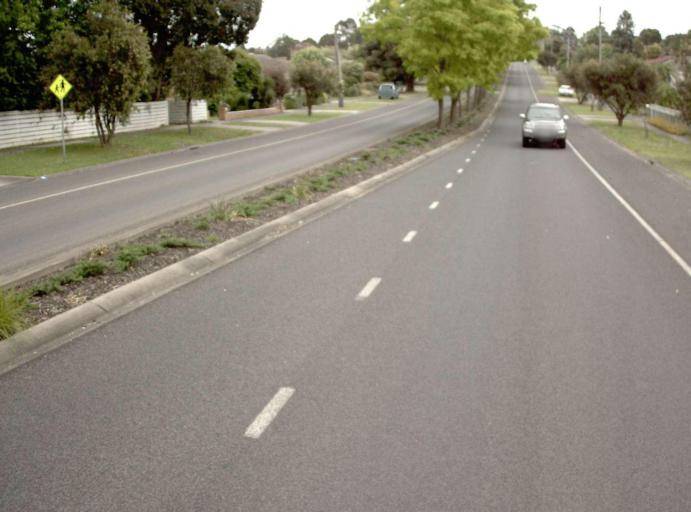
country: AU
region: Victoria
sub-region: Baw Baw
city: Warragul
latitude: -38.4850
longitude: 145.9508
